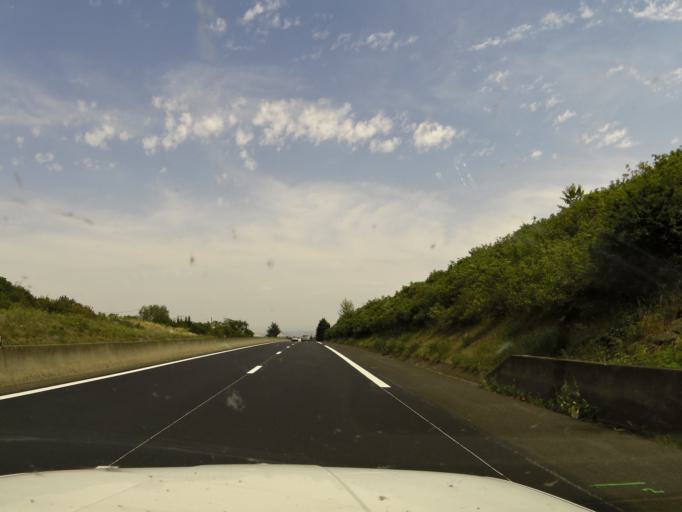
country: FR
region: Auvergne
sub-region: Departement du Puy-de-Dome
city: Aubiere
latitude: 45.7407
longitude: 3.1149
